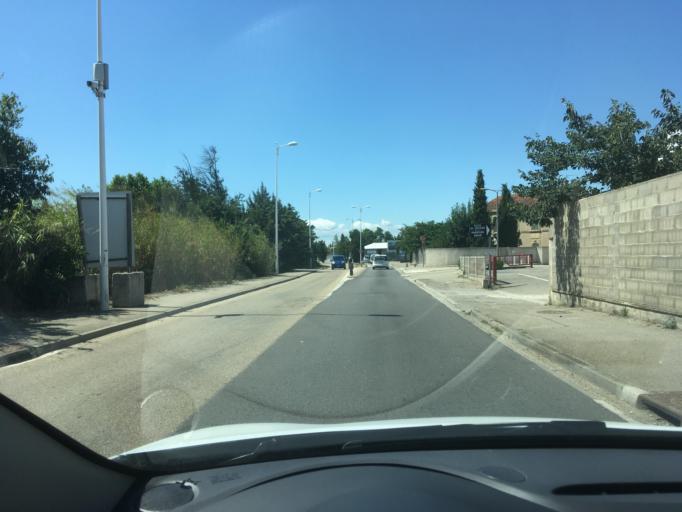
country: FR
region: Provence-Alpes-Cote d'Azur
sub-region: Departement des Bouches-du-Rhone
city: Chateaurenard
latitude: 43.8882
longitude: 4.8437
